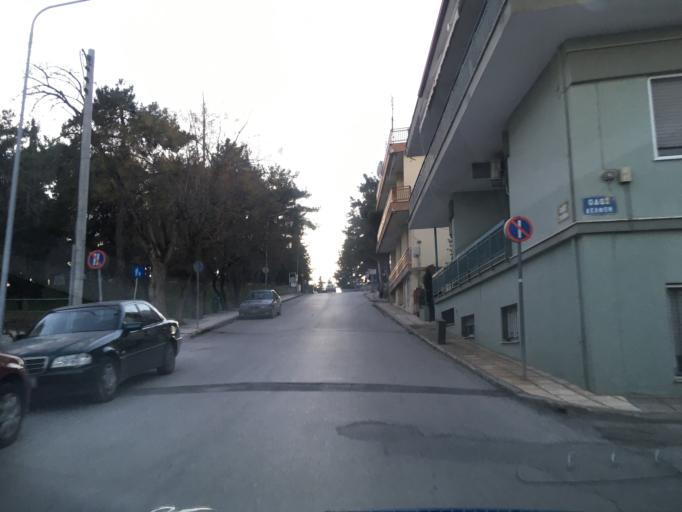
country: GR
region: West Macedonia
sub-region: Nomos Kozanis
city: Kozani
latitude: 40.3036
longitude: 21.7947
